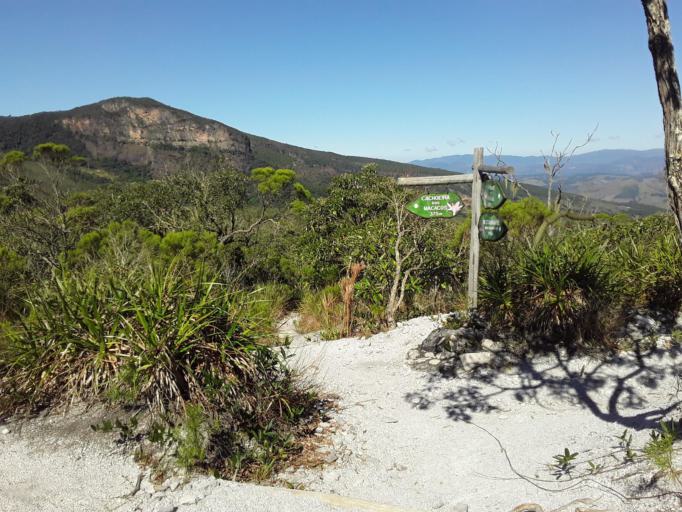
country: BR
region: Minas Gerais
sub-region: Lima Duarte
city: Lima Duarte
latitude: -21.7153
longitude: -43.8939
